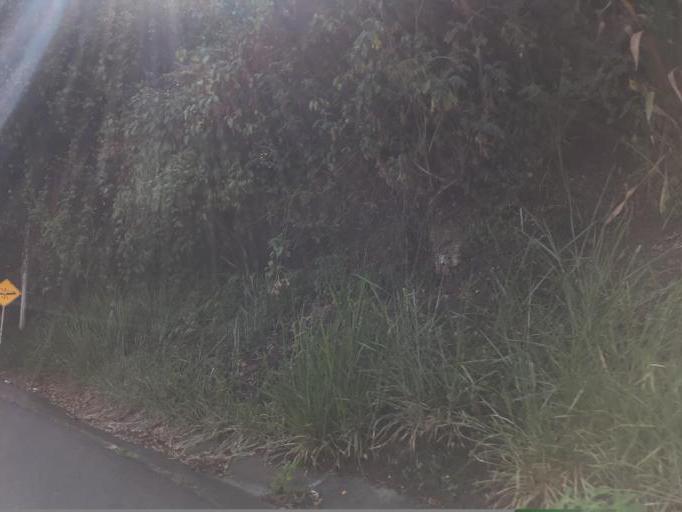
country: CO
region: Valle del Cauca
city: Cali
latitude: 3.4796
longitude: -76.6015
